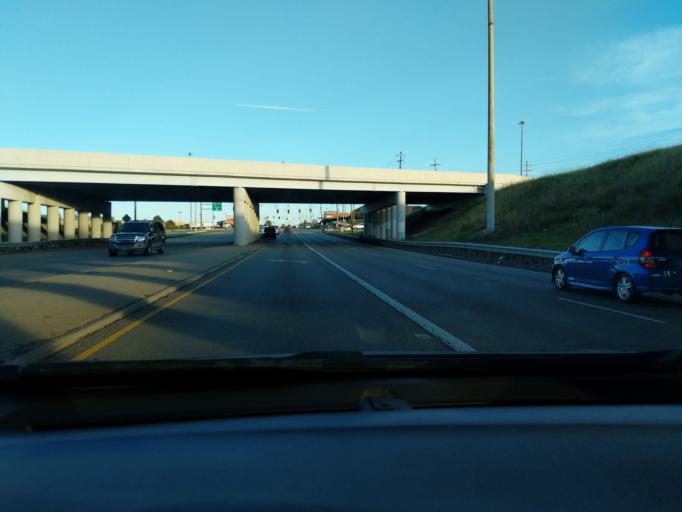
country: US
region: Ohio
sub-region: Montgomery County
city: West Carrollton City
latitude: 39.6396
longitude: -84.2320
